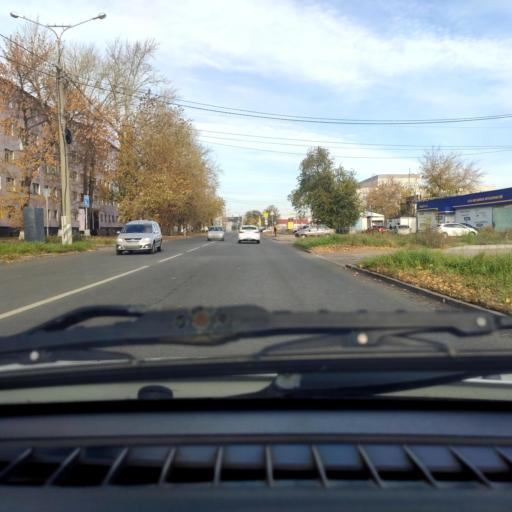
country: RU
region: Samara
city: Tol'yatti
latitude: 53.5276
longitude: 49.4301
